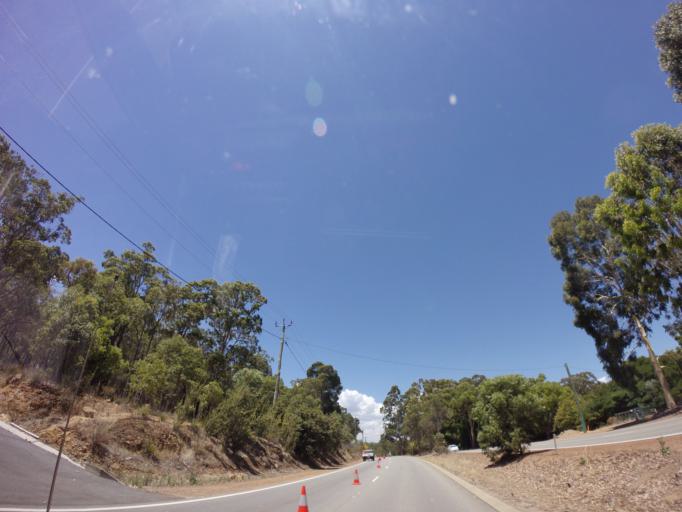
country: AU
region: Western Australia
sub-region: Mundaring
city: Mundaring
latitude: -31.9012
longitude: 116.1554
